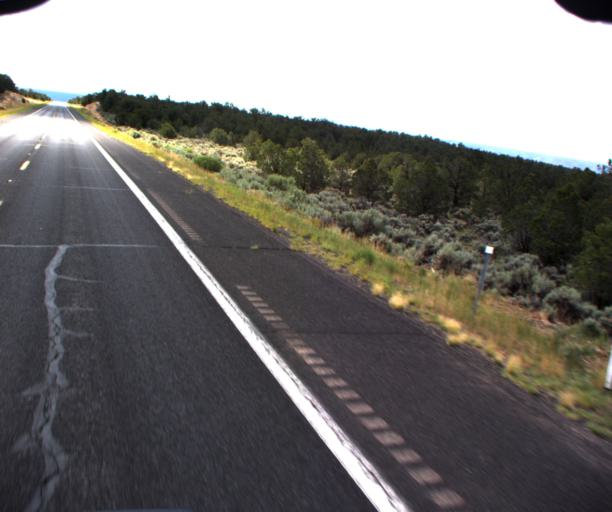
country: US
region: Arizona
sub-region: Coconino County
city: Grand Canyon
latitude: 35.9864
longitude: -111.7981
